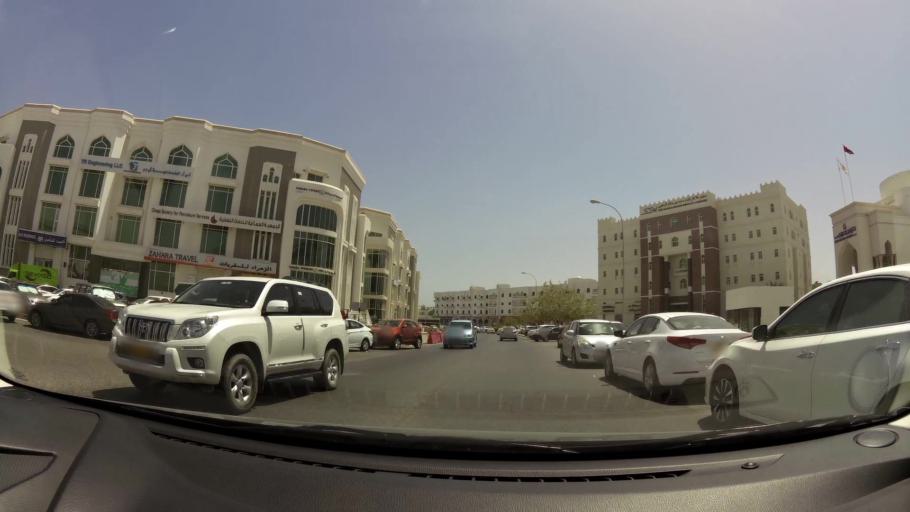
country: OM
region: Muhafazat Masqat
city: Bawshar
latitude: 23.5933
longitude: 58.4480
